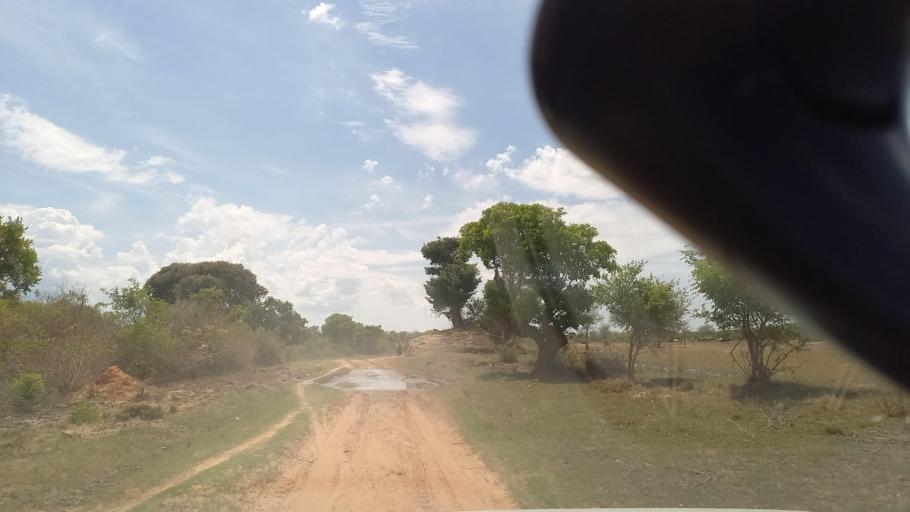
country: ZM
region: Southern
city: Mazabuka
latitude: -16.1406
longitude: 27.7639
